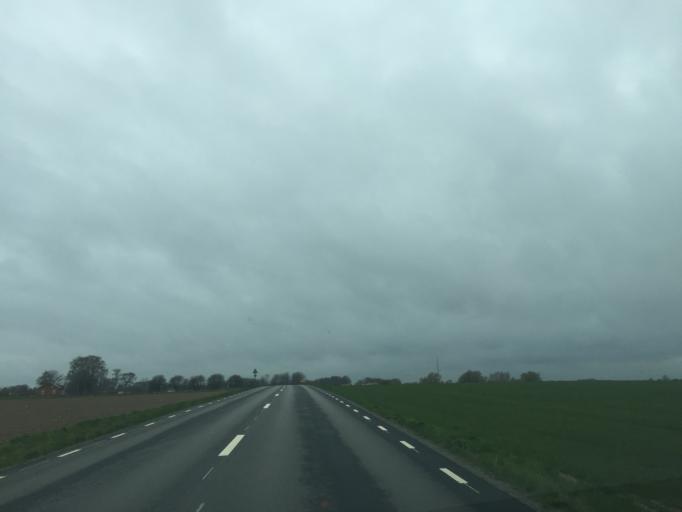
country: SE
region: Skane
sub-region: Skurups Kommun
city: Skivarp
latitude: 55.4246
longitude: 13.5924
